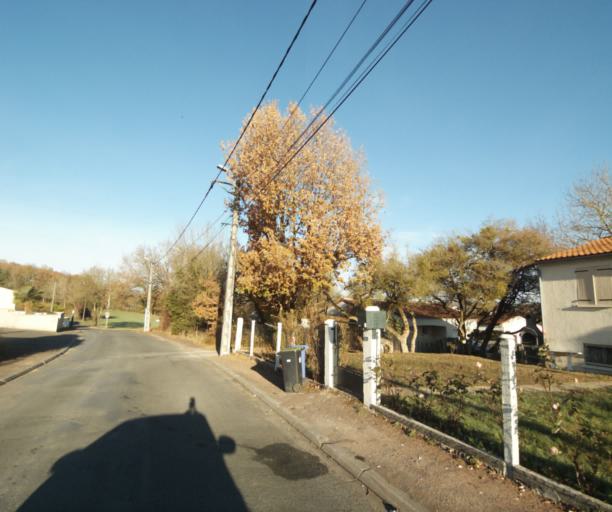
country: FR
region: Poitou-Charentes
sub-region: Departement de la Charente-Maritime
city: Fontcouverte
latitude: 45.7520
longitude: -0.6060
